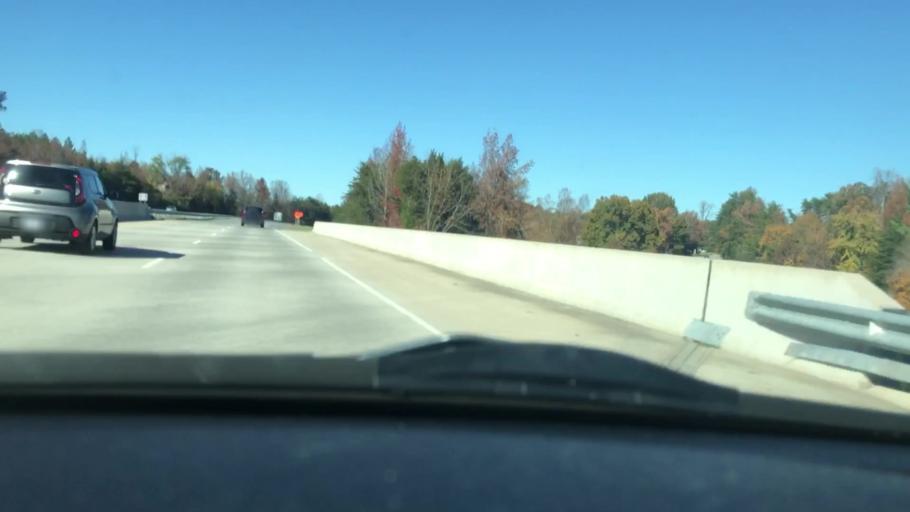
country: US
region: North Carolina
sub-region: Rockingham County
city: Stoneville
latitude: 36.4465
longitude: -79.9308
